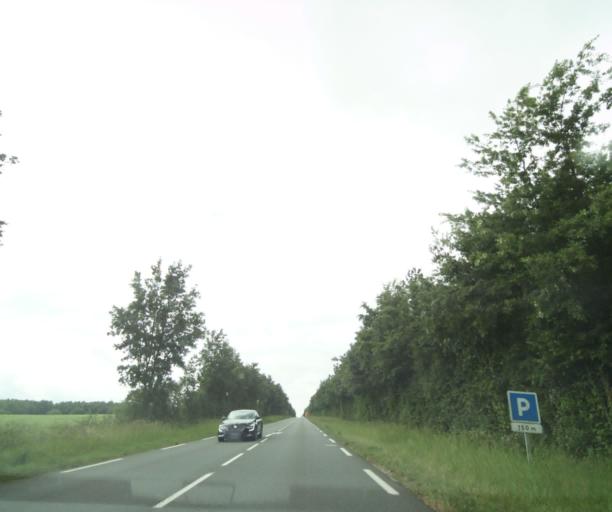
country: FR
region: Pays de la Loire
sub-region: Departement de Maine-et-Loire
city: Montreuil-Bellay
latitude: 47.1628
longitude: -0.1428
